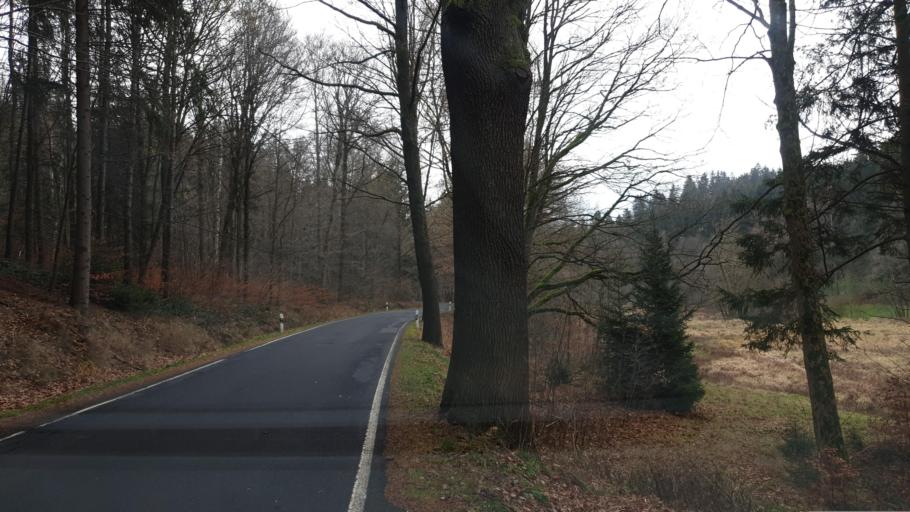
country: DE
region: Saxony
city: Mulda
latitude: 50.7897
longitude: 13.4054
